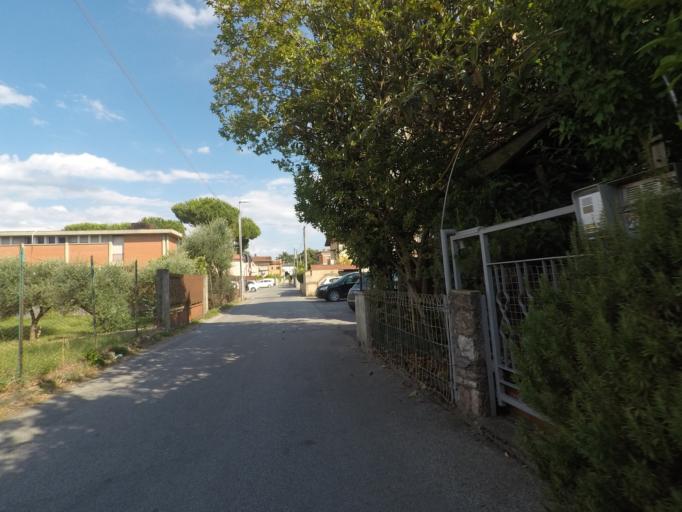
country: IT
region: Tuscany
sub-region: Provincia di Massa-Carrara
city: Massa
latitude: 44.0204
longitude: 10.1206
